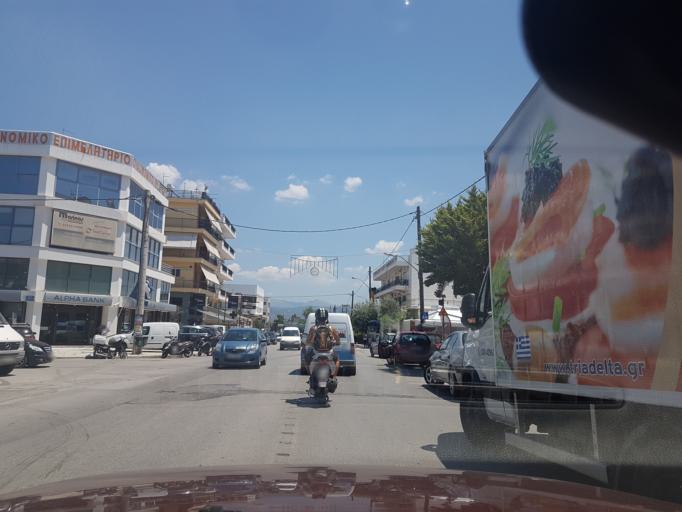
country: GR
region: Central Greece
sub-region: Nomos Evvoias
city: Chalkida
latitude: 38.4696
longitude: 23.6091
